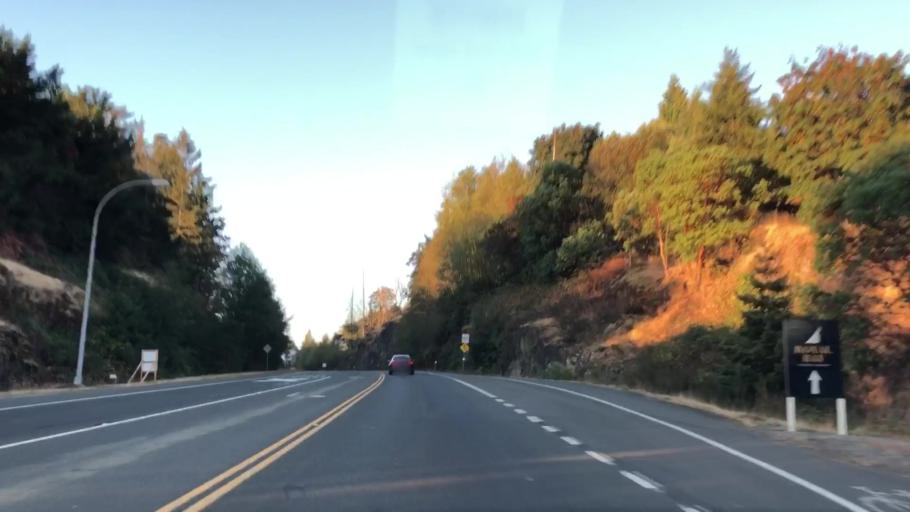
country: CA
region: British Columbia
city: Colwood
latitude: 48.4212
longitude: -123.5044
